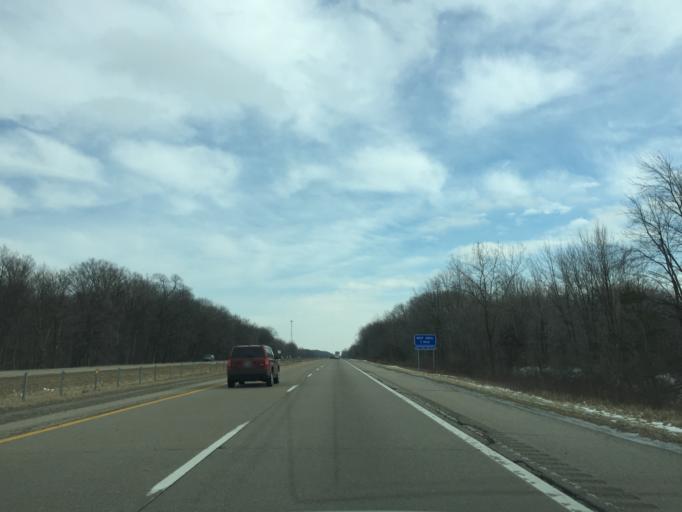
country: US
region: Michigan
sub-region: Ionia County
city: Saranac
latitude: 42.8792
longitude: -85.1871
